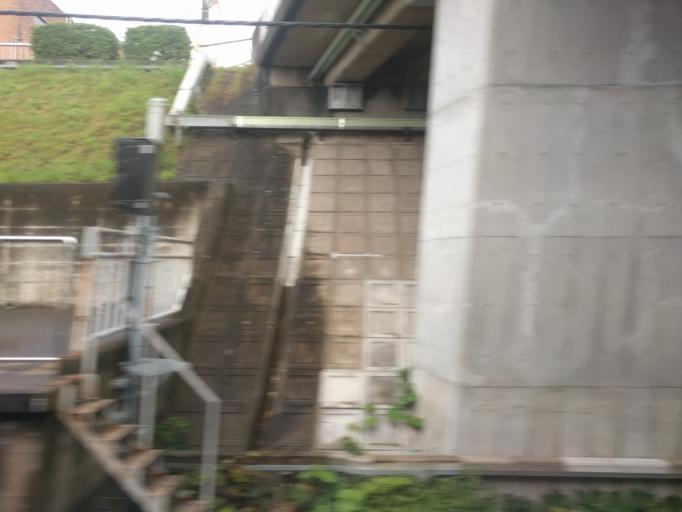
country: JP
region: Tokyo
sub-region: Machida-shi
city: Machida
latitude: 35.5281
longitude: 139.4852
